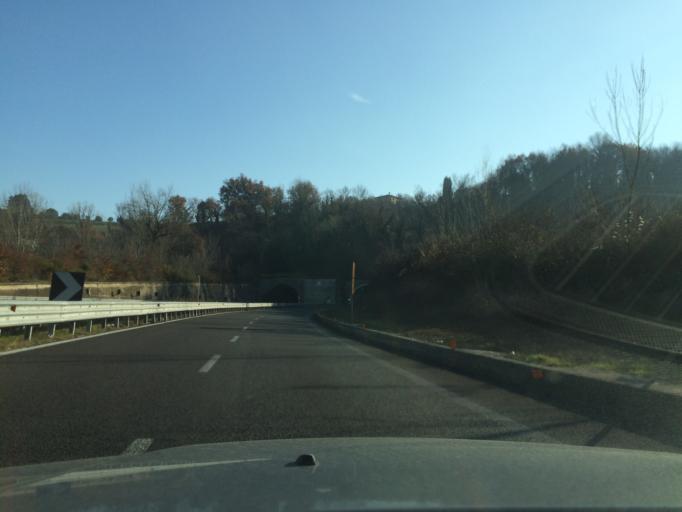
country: IT
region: Umbria
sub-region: Provincia di Perugia
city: Massa Martana
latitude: 42.7483
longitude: 12.4697
